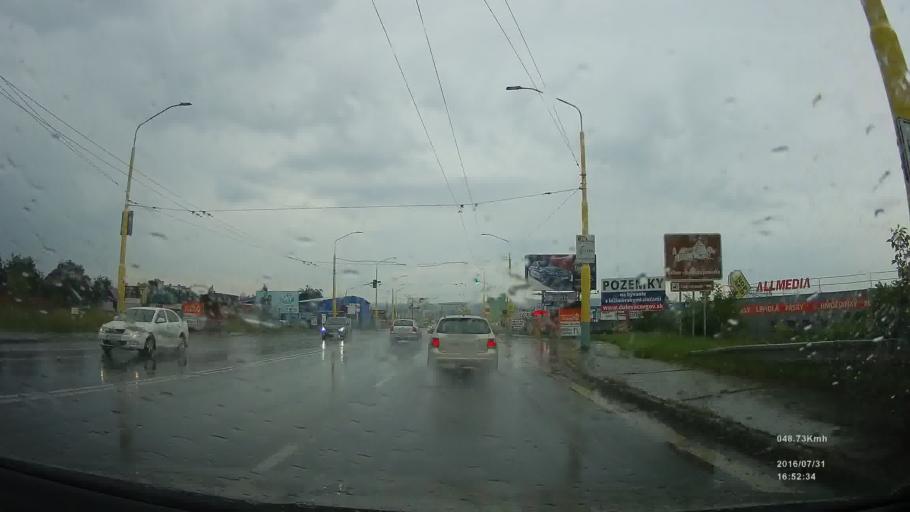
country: SK
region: Presovsky
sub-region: Okres Presov
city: Presov
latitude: 49.0185
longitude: 21.2721
